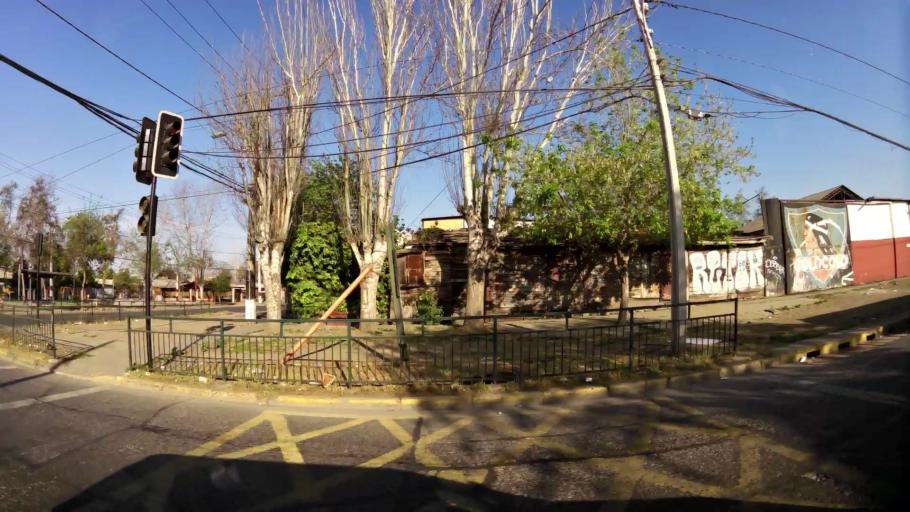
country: CL
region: Santiago Metropolitan
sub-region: Provincia de Santiago
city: Santiago
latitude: -33.3809
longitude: -70.6493
